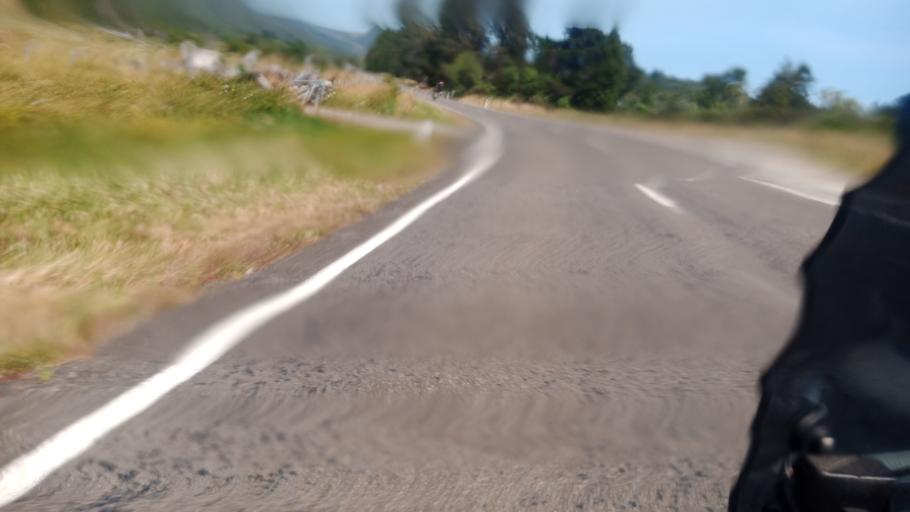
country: NZ
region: Bay of Plenty
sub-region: Opotiki District
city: Opotiki
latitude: -37.5909
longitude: 178.2156
